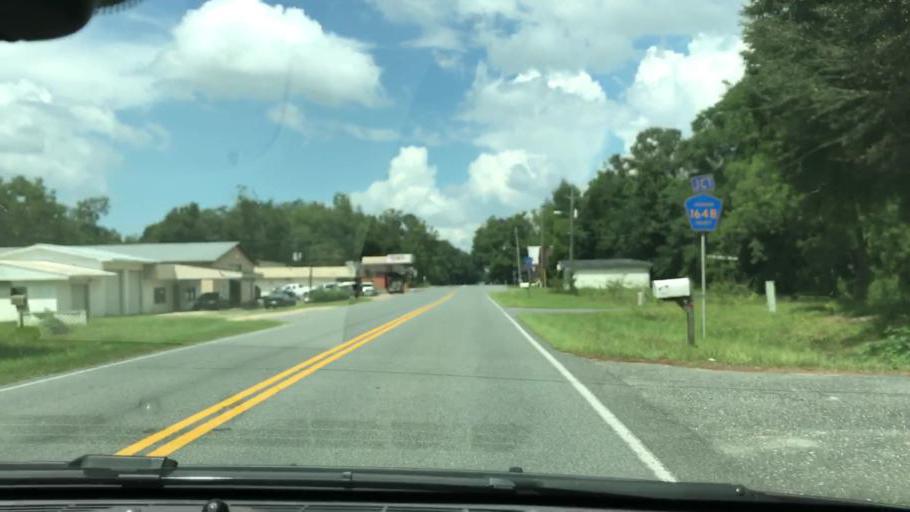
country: US
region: Florida
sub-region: Jackson County
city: Malone
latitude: 30.9254
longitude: -85.1186
